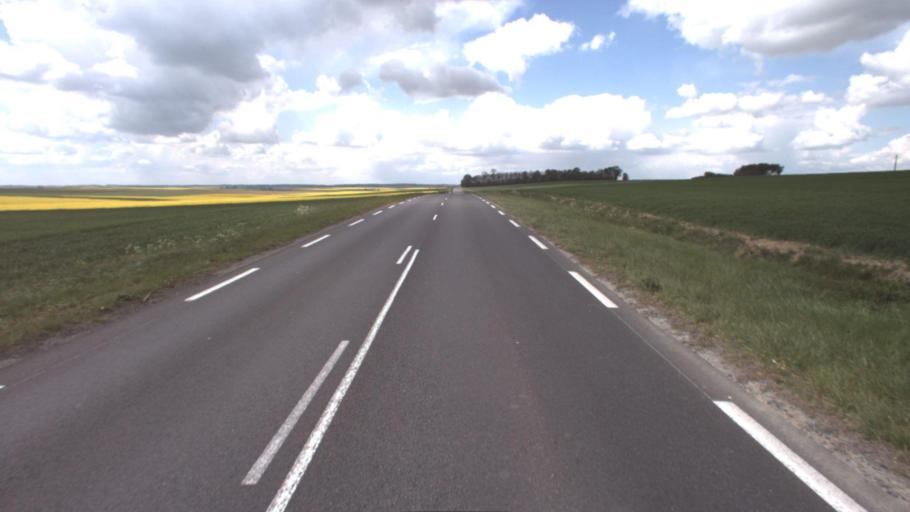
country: FR
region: Ile-de-France
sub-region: Departement de Seine-et-Marne
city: Villiers-Saint-Georges
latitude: 48.6922
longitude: 3.4232
